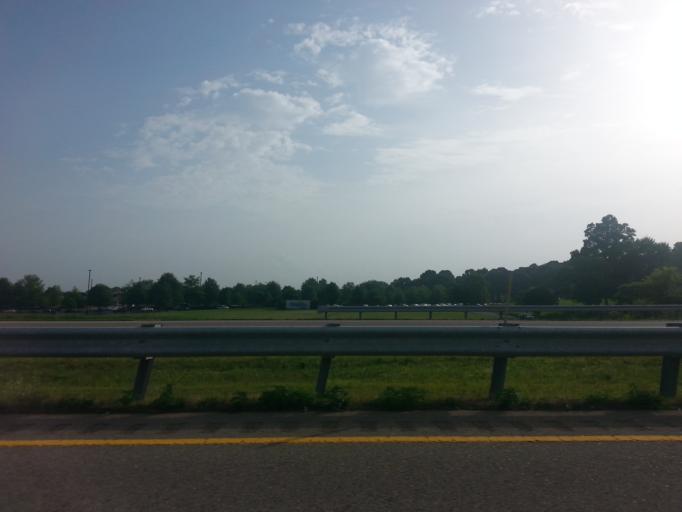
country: US
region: Tennessee
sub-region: Blount County
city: Eagleton Village
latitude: 35.8118
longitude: -83.9463
